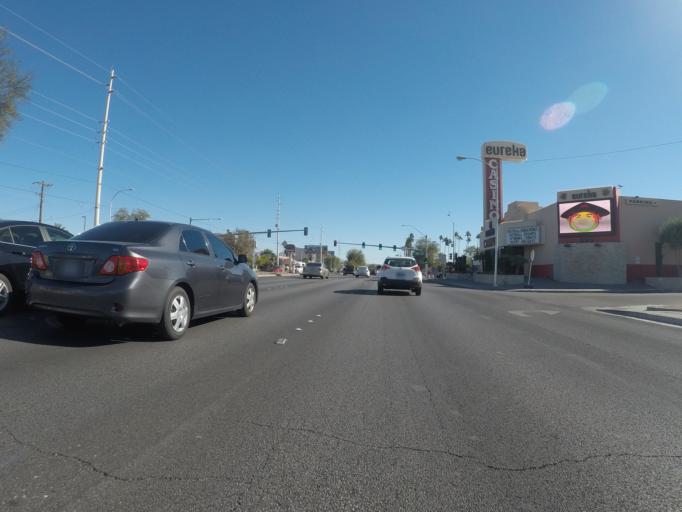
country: US
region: Nevada
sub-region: Clark County
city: Winchester
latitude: 36.1438
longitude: -115.1475
